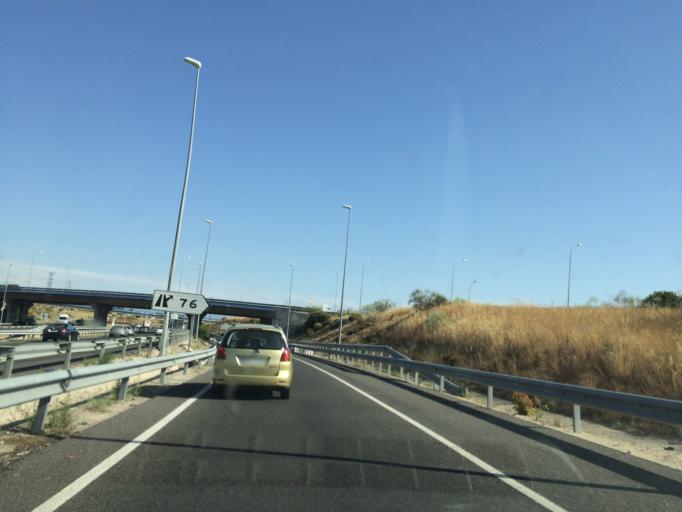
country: ES
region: Madrid
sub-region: Provincia de Madrid
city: Majadahonda
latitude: 40.4415
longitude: -3.8774
